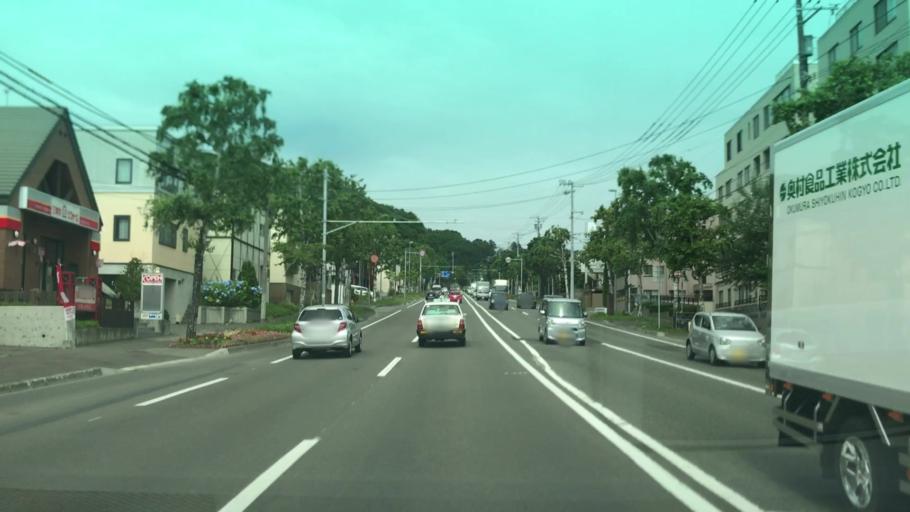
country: JP
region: Hokkaido
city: Sapporo
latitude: 43.0626
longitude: 141.2934
